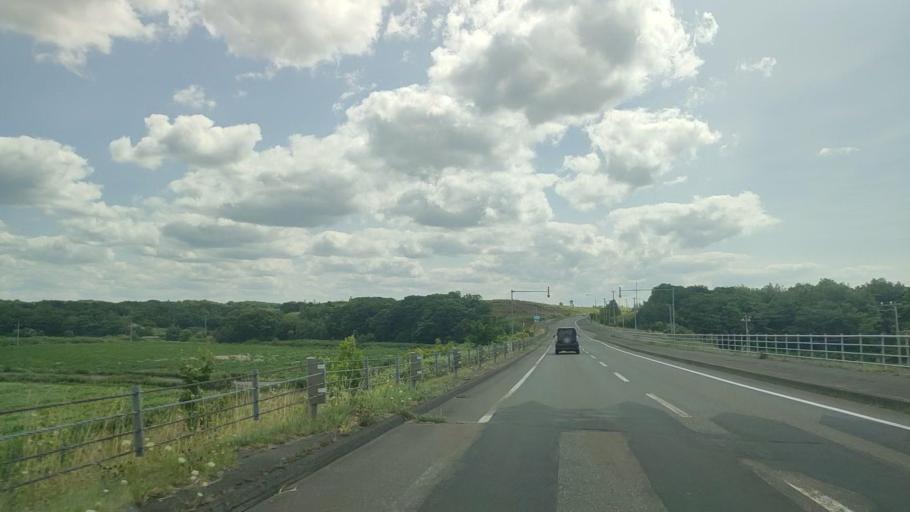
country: JP
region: Hokkaido
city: Makubetsu
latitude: 44.7944
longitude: 141.7894
